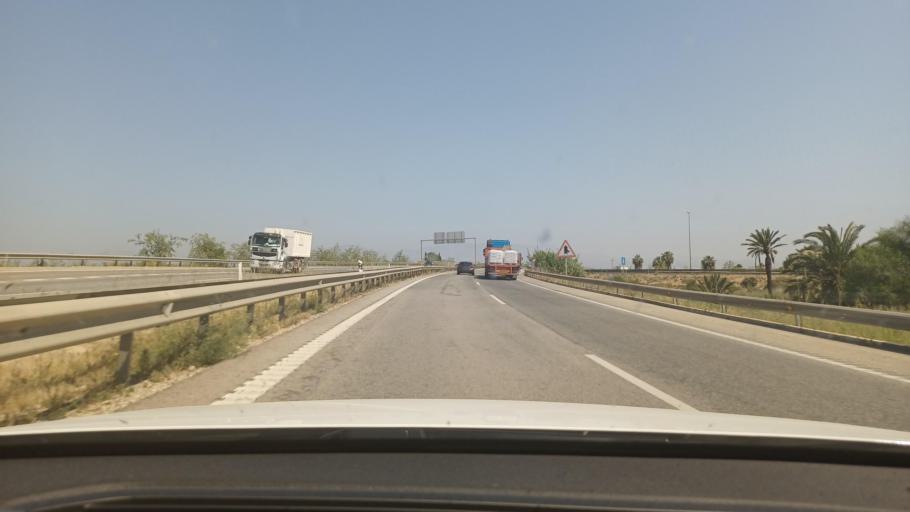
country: ES
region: Valencia
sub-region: Provincia de Alicante
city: Catral
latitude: 38.1489
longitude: -0.8196
